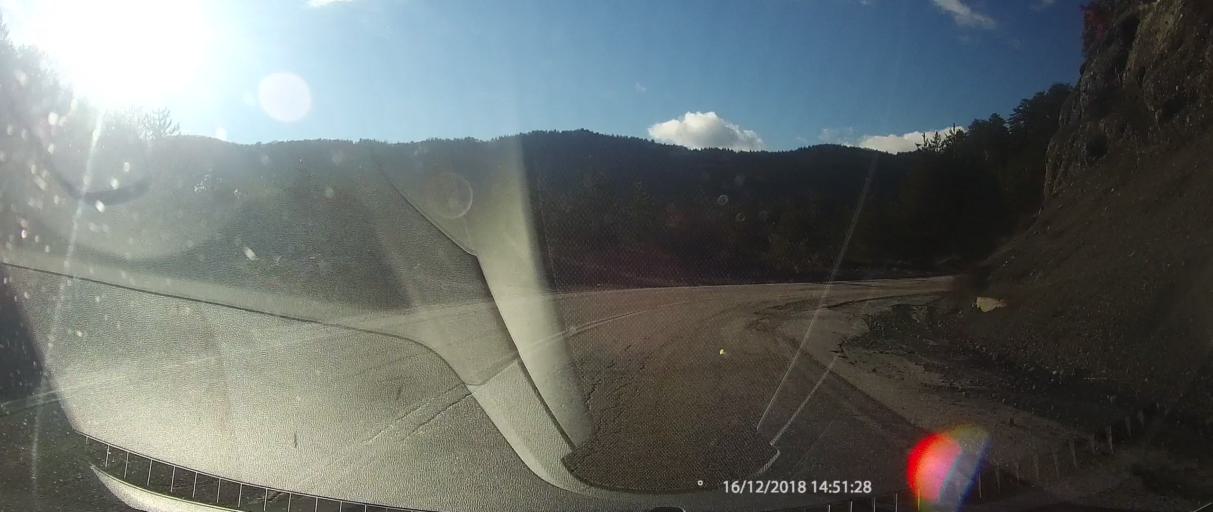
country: GR
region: West Macedonia
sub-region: Nomos Kastorias
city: Nestorio
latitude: 40.2039
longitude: 21.0724
